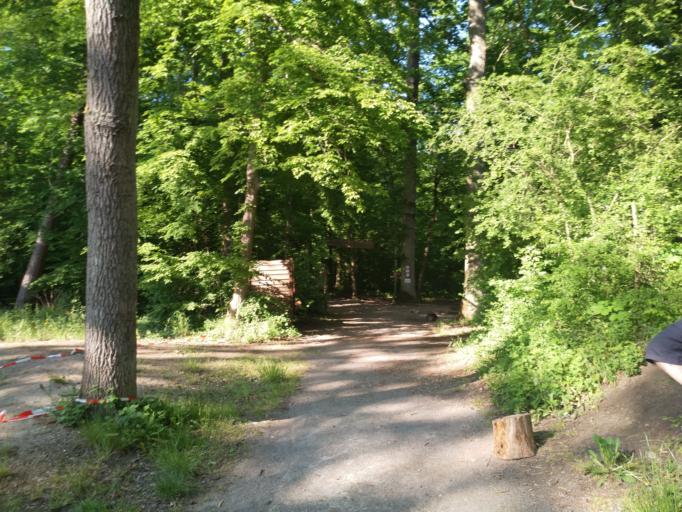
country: DE
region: Baden-Wuerttemberg
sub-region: Karlsruhe Region
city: Otisheim
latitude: 48.9697
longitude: 8.7996
